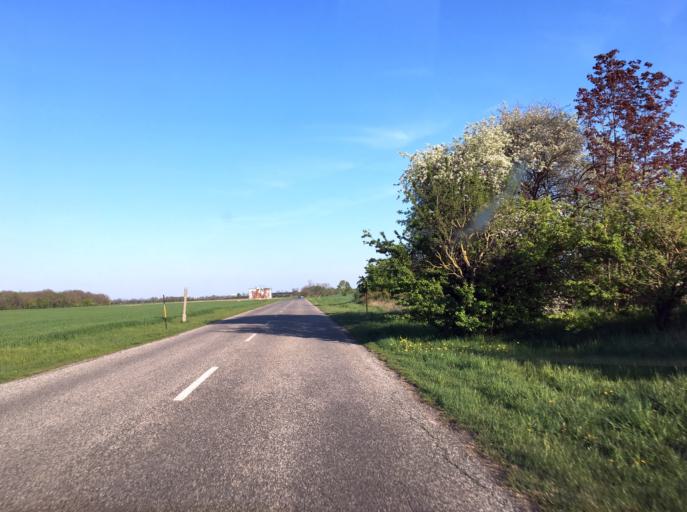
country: AT
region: Burgenland
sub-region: Politischer Bezirk Neusiedl am See
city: Kittsee
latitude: 48.0778
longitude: 17.0799
